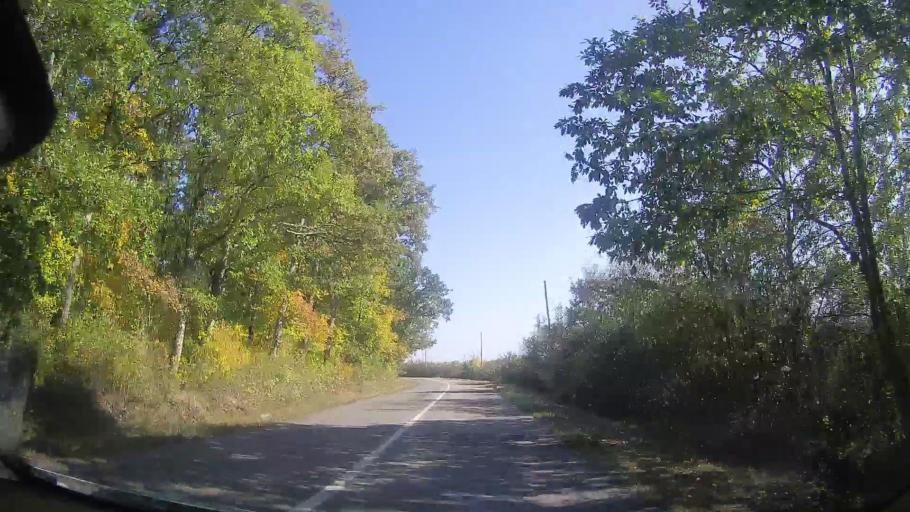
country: RO
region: Timis
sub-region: Comuna Ghizela
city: Ghizela
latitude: 45.8382
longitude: 21.7775
